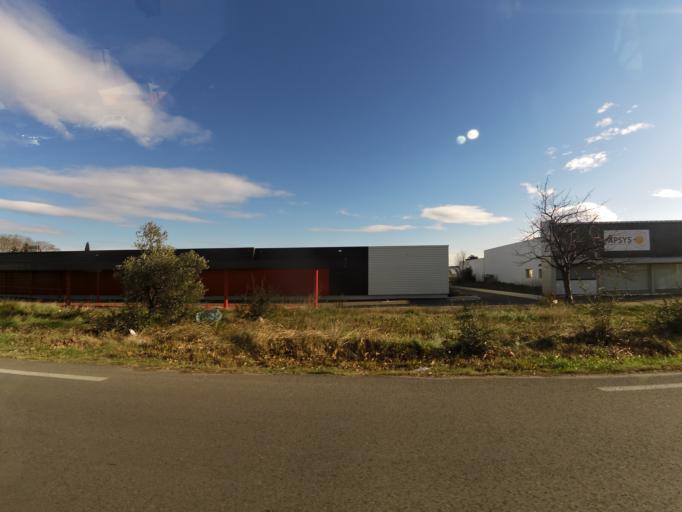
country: FR
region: Languedoc-Roussillon
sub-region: Departement du Gard
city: Milhaud
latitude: 43.8068
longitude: 4.3243
